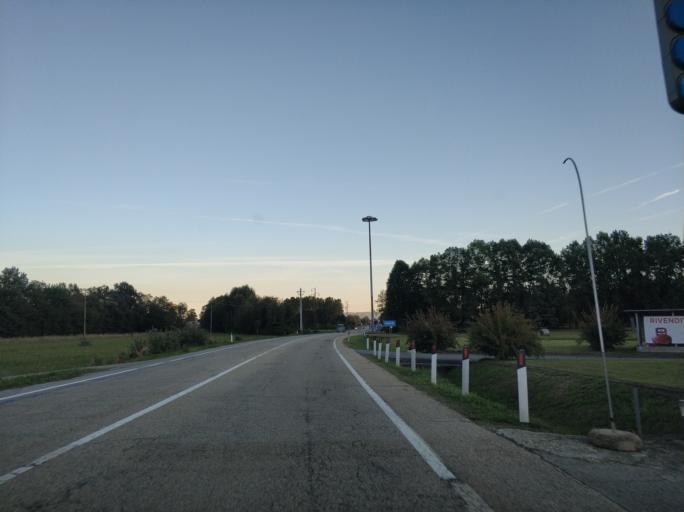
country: IT
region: Piedmont
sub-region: Provincia di Torino
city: Fiano
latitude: 45.2140
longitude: 7.5437
